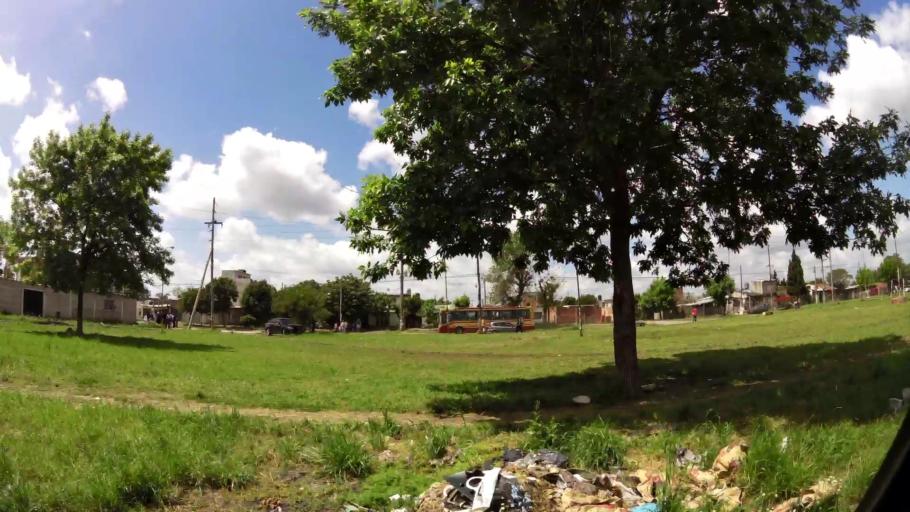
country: AR
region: Buenos Aires
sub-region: Partido de Quilmes
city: Quilmes
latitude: -34.8333
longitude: -58.2341
